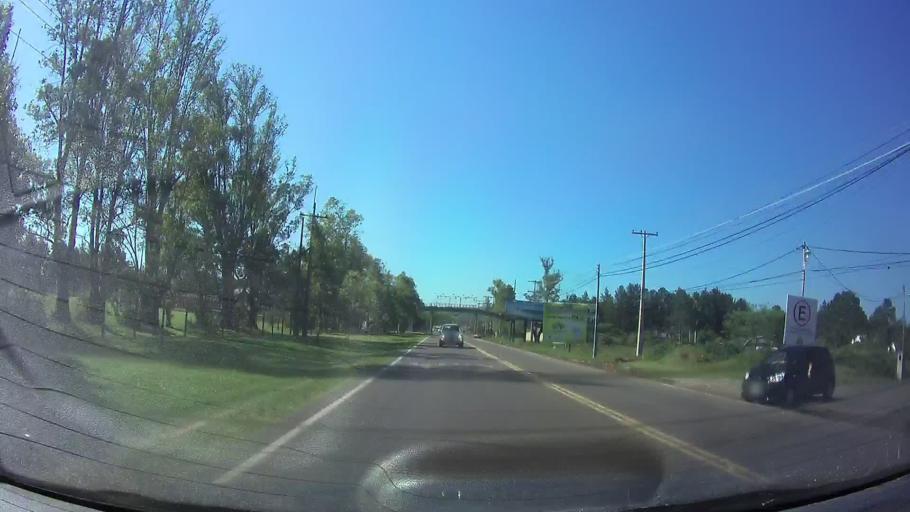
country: PY
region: Cordillera
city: San Bernardino
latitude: -25.3407
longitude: -57.2738
